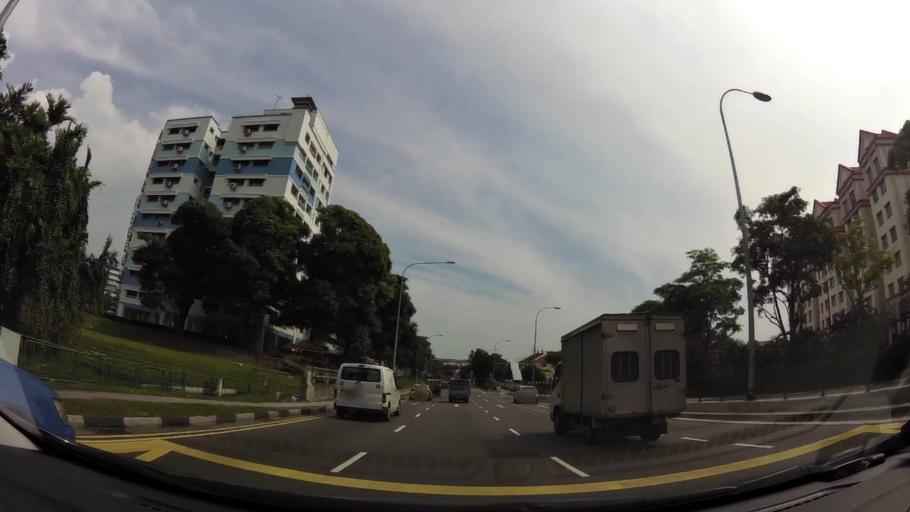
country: SG
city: Singapore
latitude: 1.3611
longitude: 103.9619
